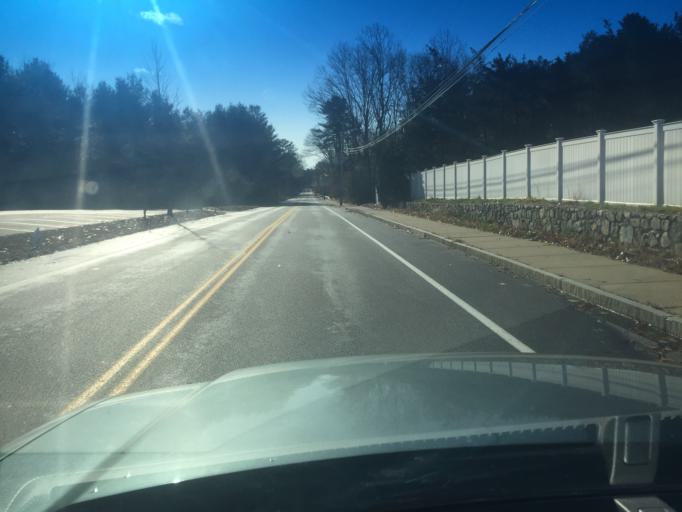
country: US
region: Massachusetts
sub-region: Norfolk County
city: Medway
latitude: 42.1268
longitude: -71.4312
